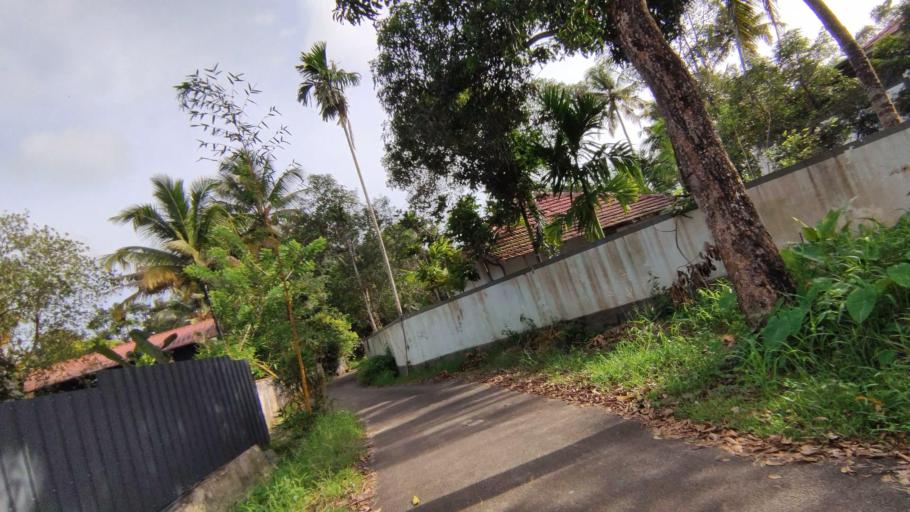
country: IN
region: Kerala
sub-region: Alappuzha
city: Shertallai
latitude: 9.6321
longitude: 76.3349
